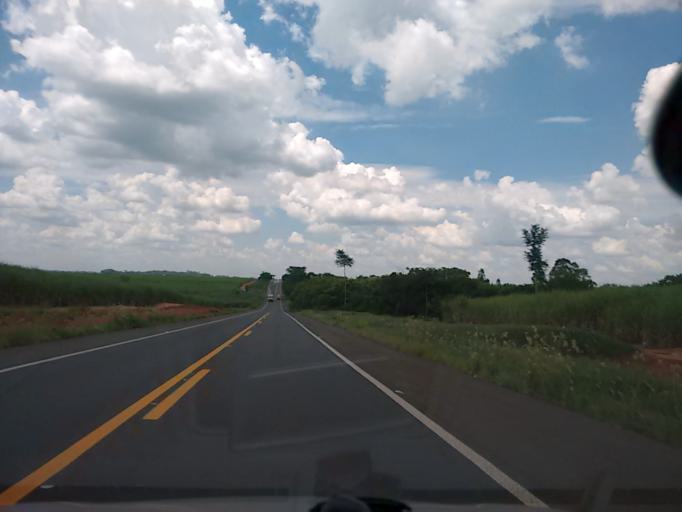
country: BR
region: Sao Paulo
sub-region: Osvaldo Cruz
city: Osvaldo Cruz
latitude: -21.8998
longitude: -50.8814
